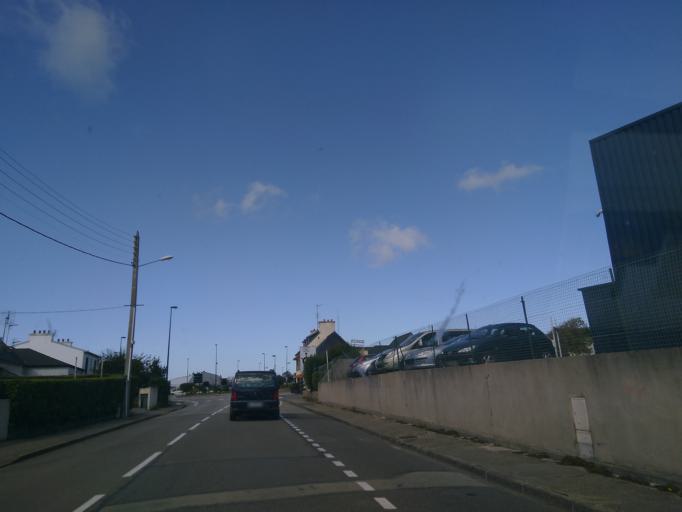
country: FR
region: Brittany
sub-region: Departement du Finistere
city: Crozon
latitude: 48.2469
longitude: -4.4987
